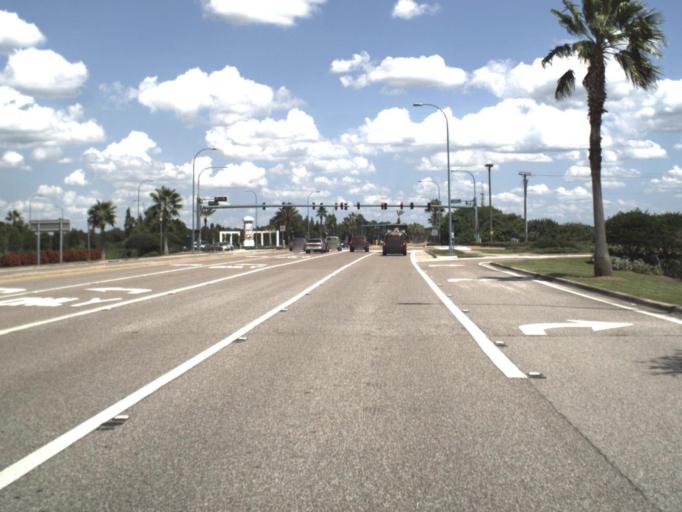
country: US
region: Florida
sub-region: Hillsborough County
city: Brandon
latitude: 27.9282
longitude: -82.3141
